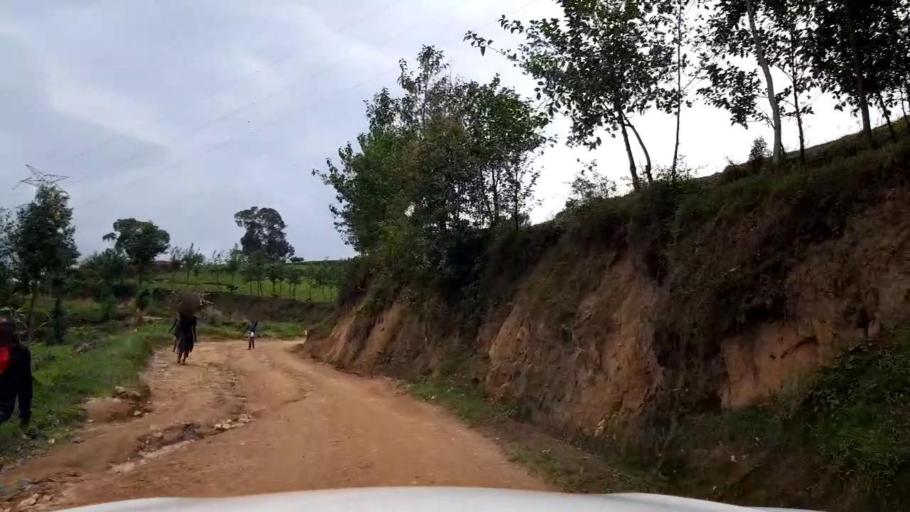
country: RW
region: Western Province
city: Kibuye
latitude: -1.9630
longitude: 29.3945
